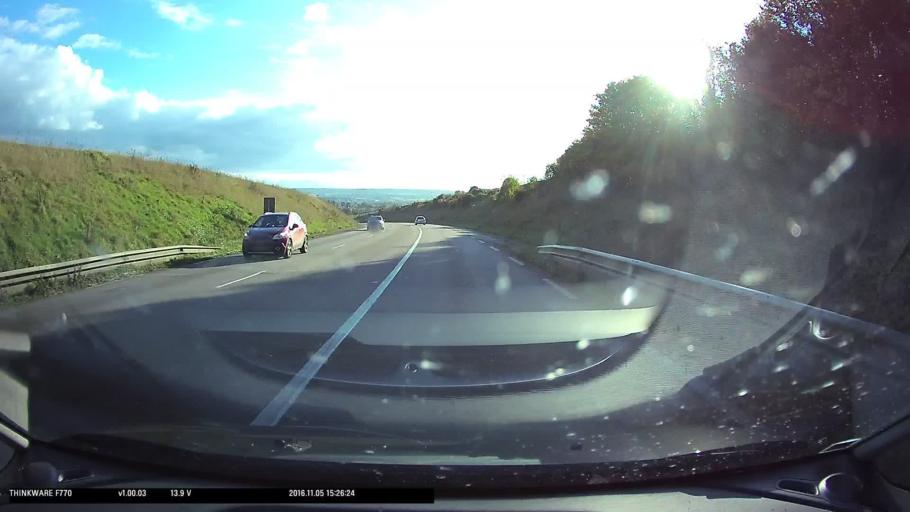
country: FR
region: Ile-de-France
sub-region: Departement des Yvelines
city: Meulan-en-Yvelines
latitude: 49.0246
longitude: 1.9104
